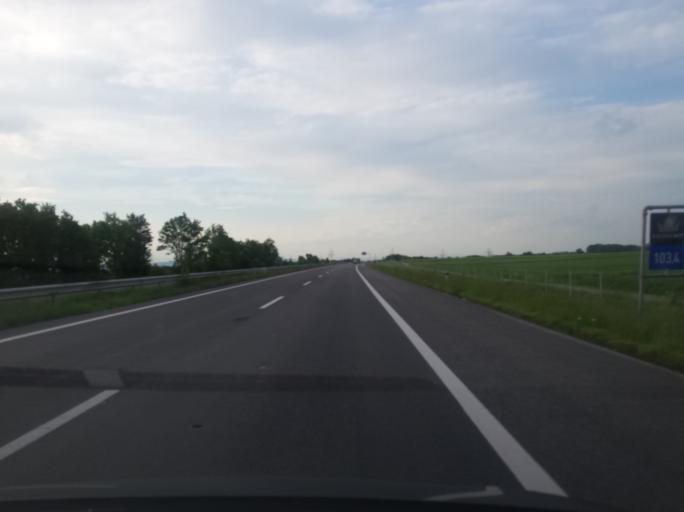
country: AT
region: Burgenland
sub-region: Eisenstadt-Umgebung
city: Steinbrunn
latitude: 47.8584
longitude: 16.4230
